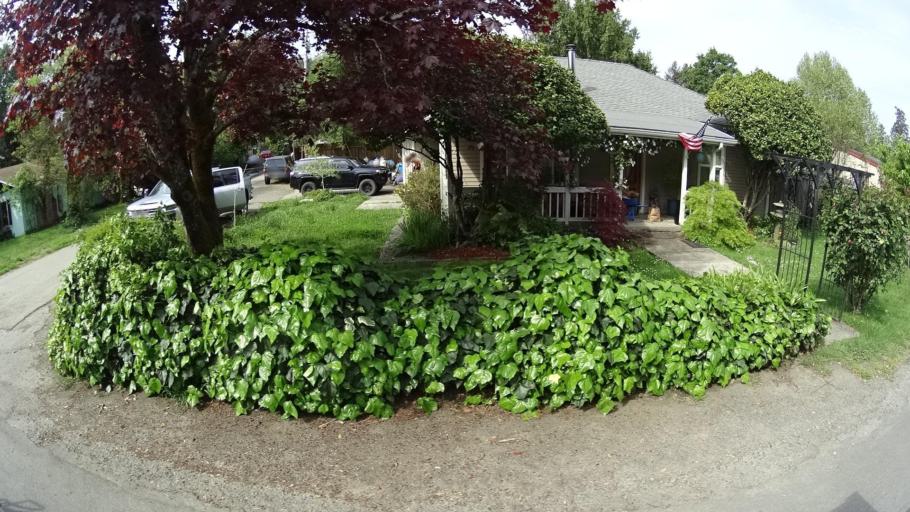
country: US
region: California
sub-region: Humboldt County
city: Redway
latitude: 40.1186
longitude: -123.8267
